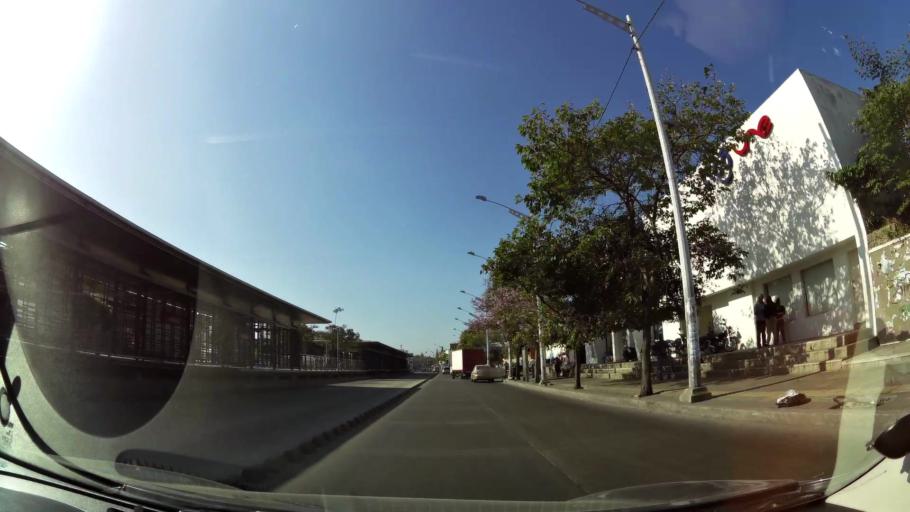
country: CO
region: Atlantico
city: Barranquilla
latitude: 10.9826
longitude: -74.7865
